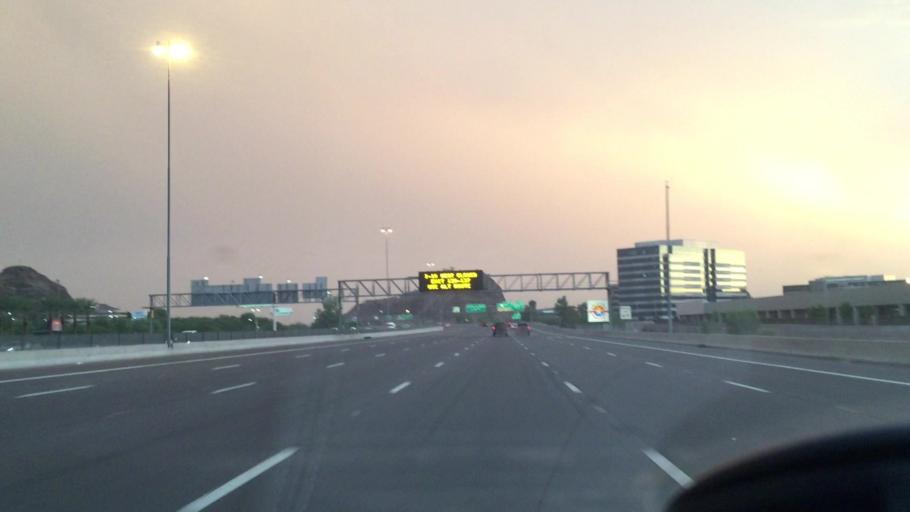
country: US
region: Arizona
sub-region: Maricopa County
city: Tempe Junction
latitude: 33.3995
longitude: -111.9661
